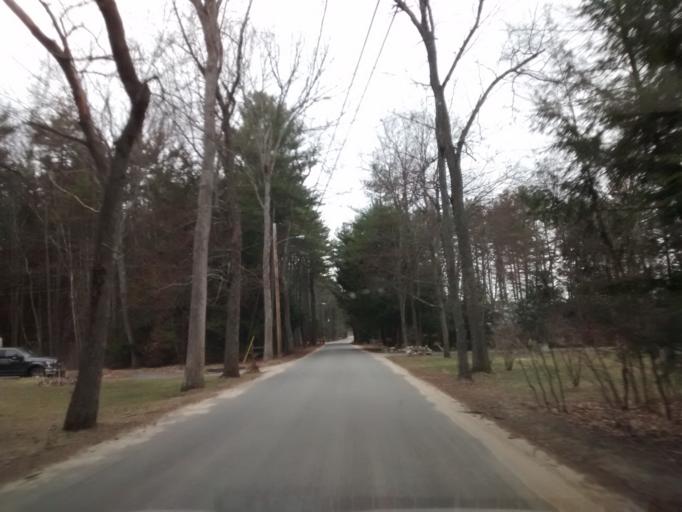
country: US
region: Massachusetts
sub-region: Franklin County
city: Orange
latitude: 42.5440
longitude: -72.2913
